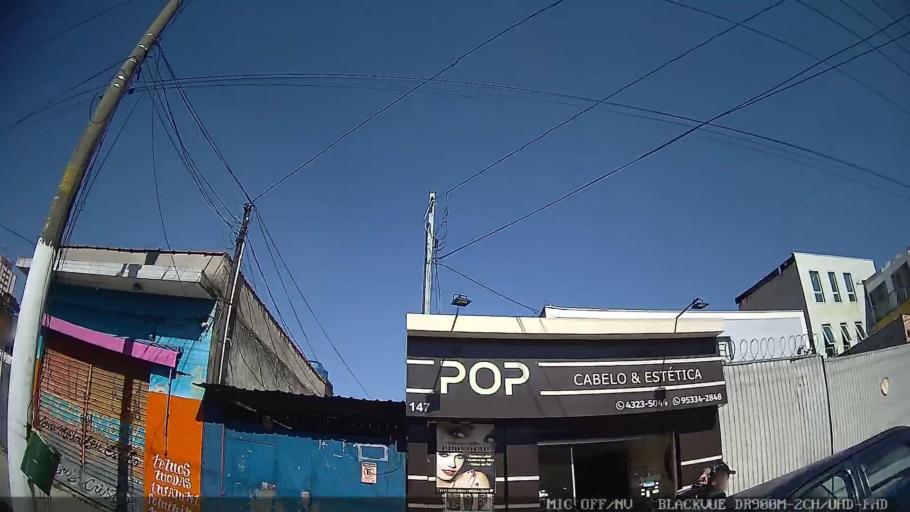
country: BR
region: Sao Paulo
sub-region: Ferraz De Vasconcelos
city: Ferraz de Vasconcelos
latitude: -23.5519
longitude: -46.4627
